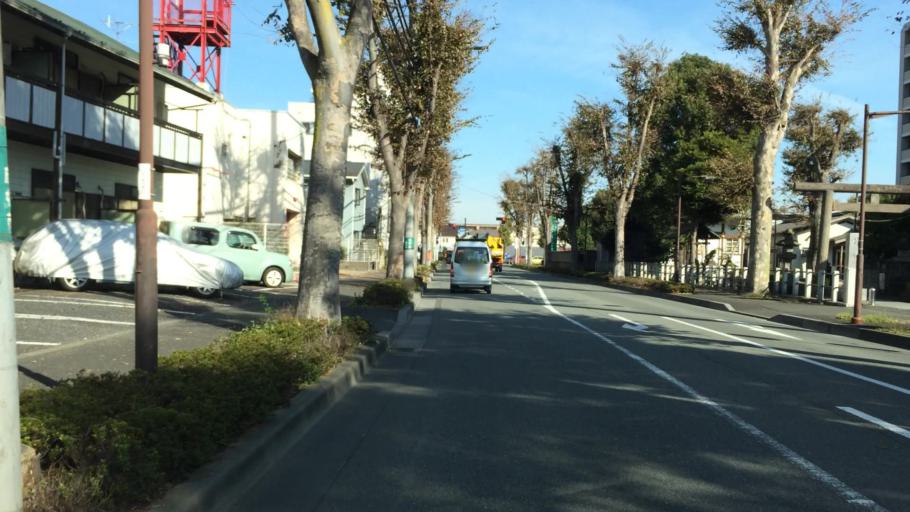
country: JP
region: Tokyo
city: Chofugaoka
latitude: 35.6661
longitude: 139.5151
